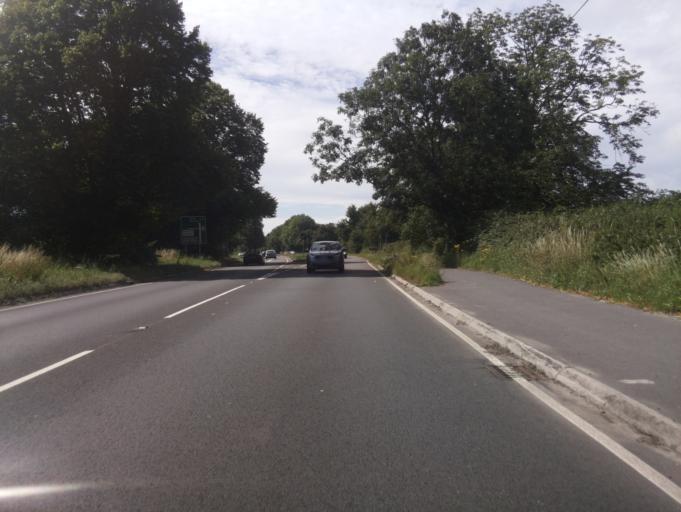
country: GB
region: England
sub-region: Dorset
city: Dorchester
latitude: 50.7385
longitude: -2.4804
